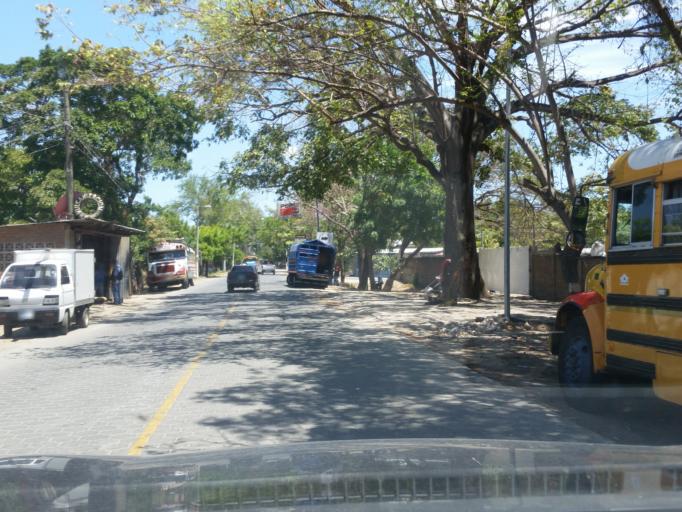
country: NI
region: Rivas
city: Rivas
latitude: 11.4423
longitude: -85.8343
